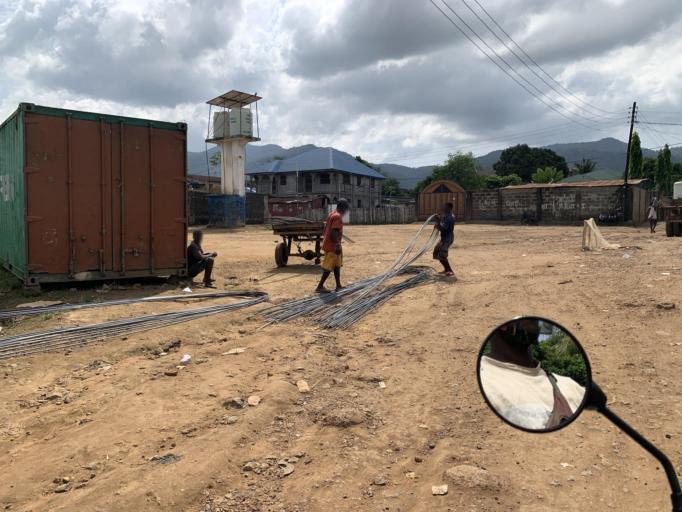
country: SL
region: Western Area
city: Hastings
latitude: 8.3929
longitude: -13.1427
